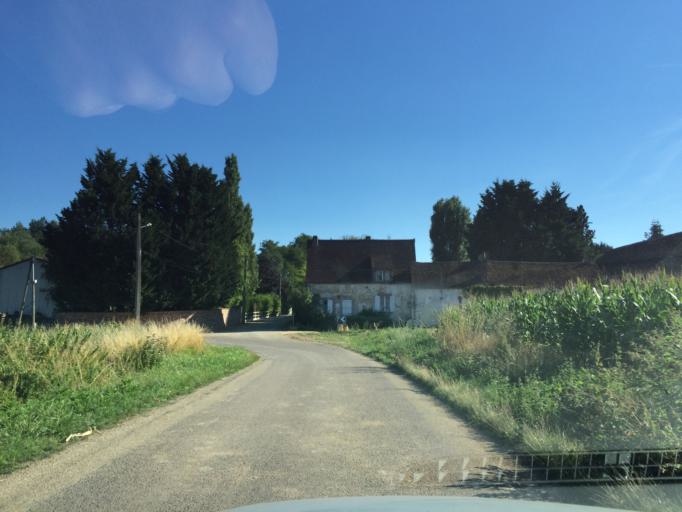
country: FR
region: Bourgogne
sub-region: Departement de l'Yonne
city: Fleury-la-Vallee
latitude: 47.9042
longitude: 3.4417
